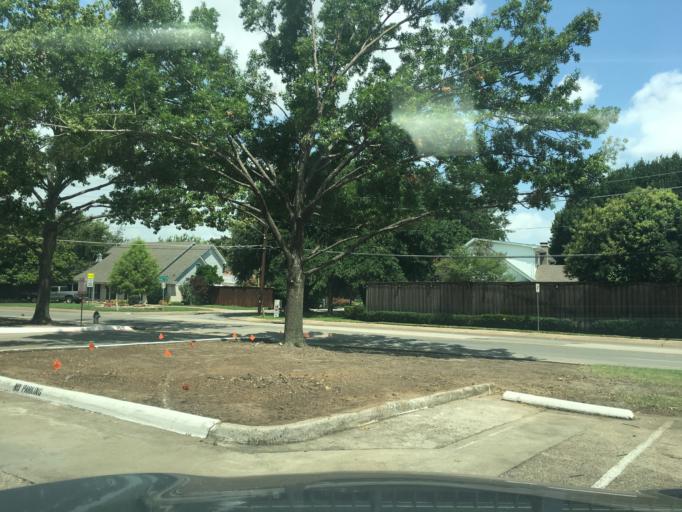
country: US
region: Texas
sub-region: Dallas County
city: Addison
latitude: 32.9212
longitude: -96.8205
